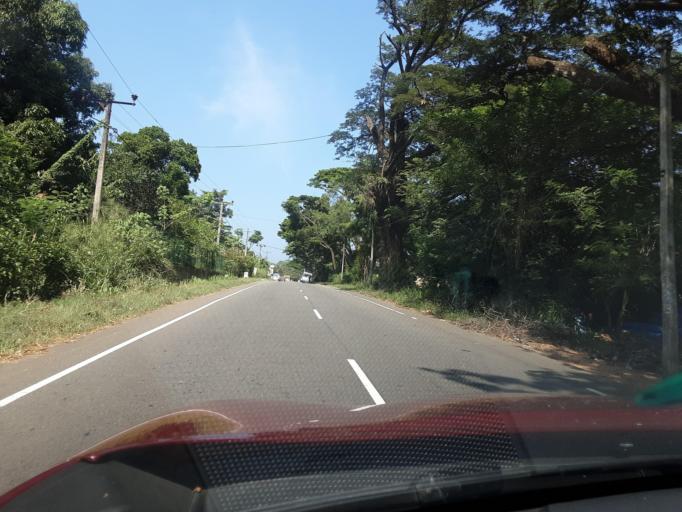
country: LK
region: Uva
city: Badulla
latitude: 7.1845
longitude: 81.0431
